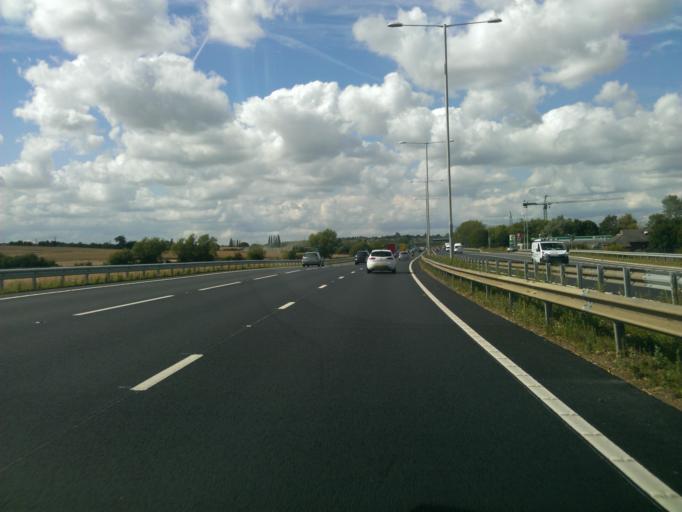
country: GB
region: England
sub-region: Northamptonshire
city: Kettering
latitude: 52.3761
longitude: -0.7251
